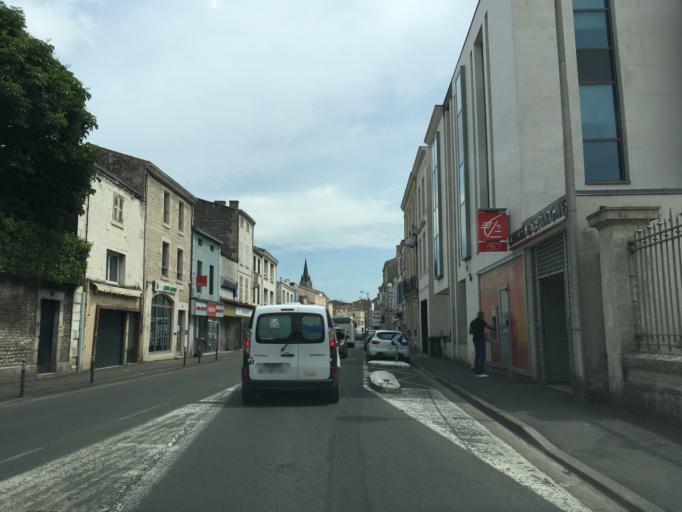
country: FR
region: Poitou-Charentes
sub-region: Departement des Deux-Sevres
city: Niort
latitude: 46.3212
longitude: -0.4630
